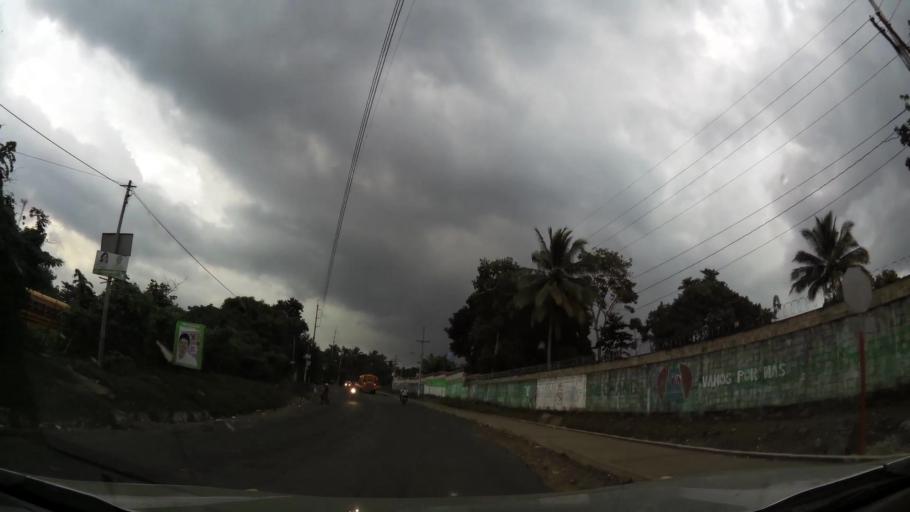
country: GT
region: Escuintla
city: Santa Lucia Cotzumalguapa
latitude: 14.3268
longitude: -91.0319
